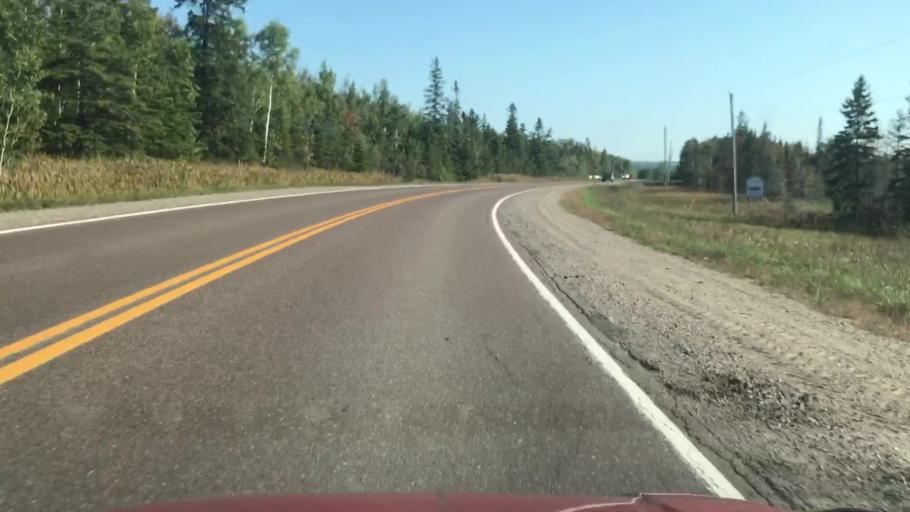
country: CA
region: Ontario
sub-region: Algoma
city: Sault Ste. Marie
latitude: 46.3346
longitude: -84.0058
